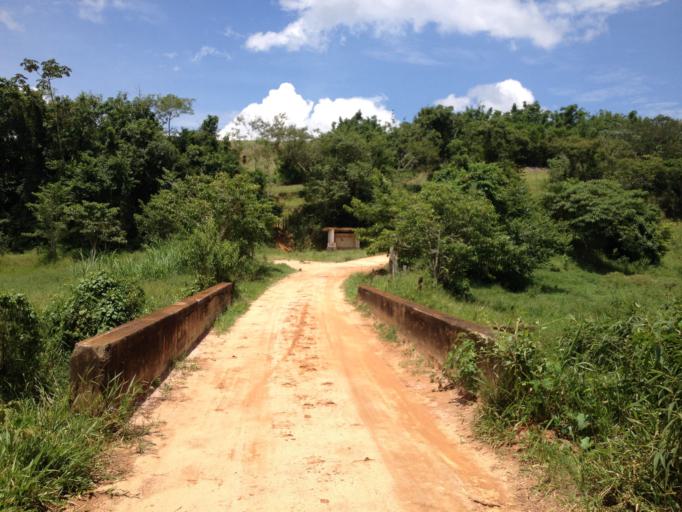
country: BR
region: Rio de Janeiro
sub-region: Valenca
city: Valenca
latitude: -22.2278
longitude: -43.8333
